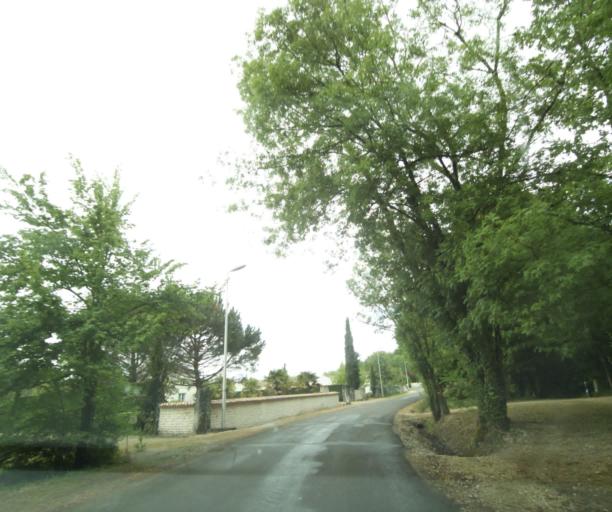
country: FR
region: Poitou-Charentes
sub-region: Departement de la Charente-Maritime
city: Cherac
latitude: 45.6828
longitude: -0.4902
